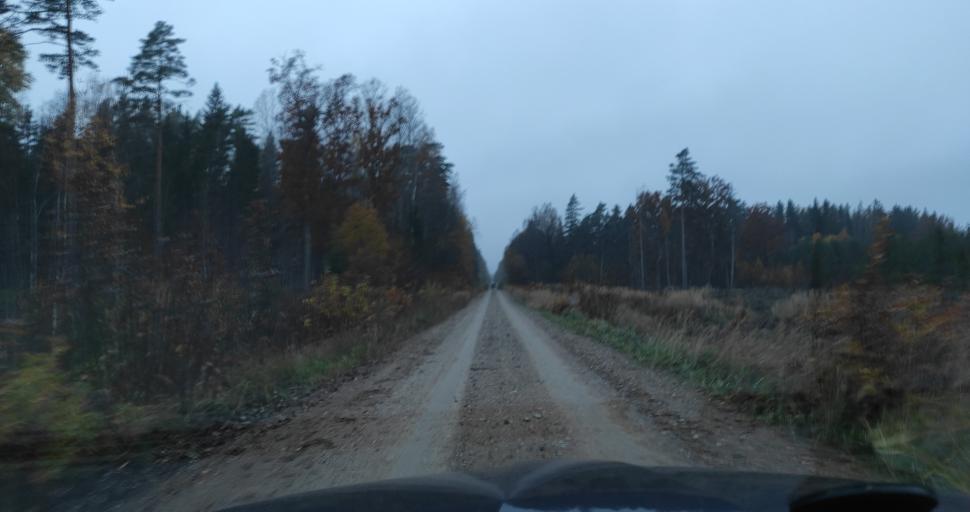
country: LV
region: Pavilostas
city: Pavilosta
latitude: 56.7465
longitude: 21.2818
